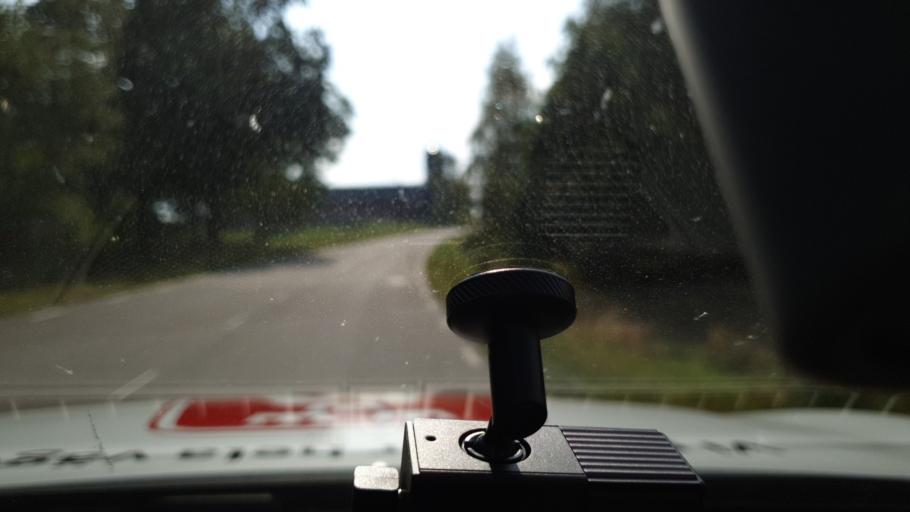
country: SE
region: Kalmar
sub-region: Vimmerby Kommun
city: Sodra Vi
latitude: 57.7184
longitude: 15.8377
